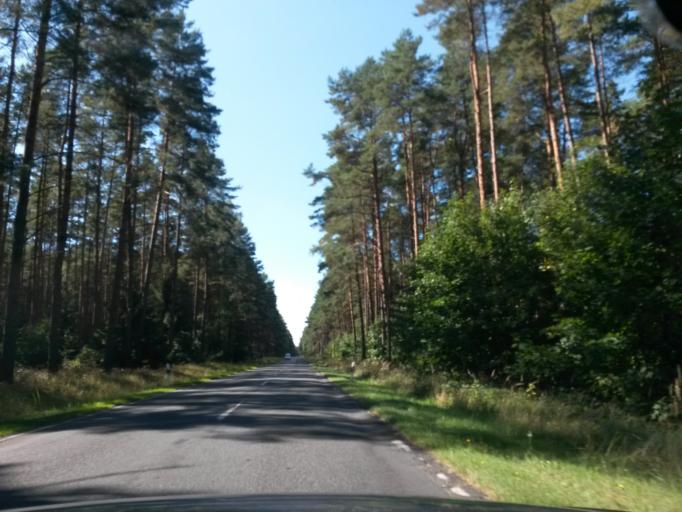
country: DE
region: Brandenburg
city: Lychen
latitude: 53.2270
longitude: 13.3656
